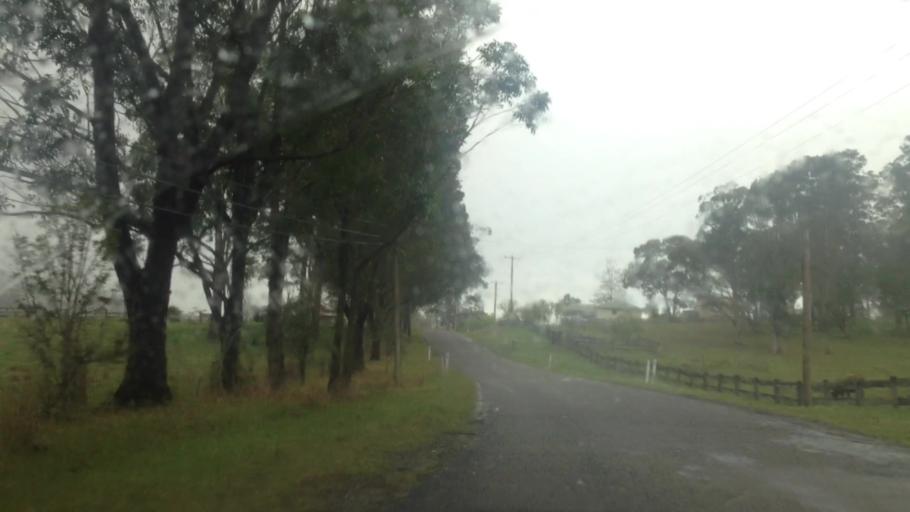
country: AU
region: New South Wales
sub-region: Wyong Shire
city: Little Jilliby
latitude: -33.1962
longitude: 151.3587
